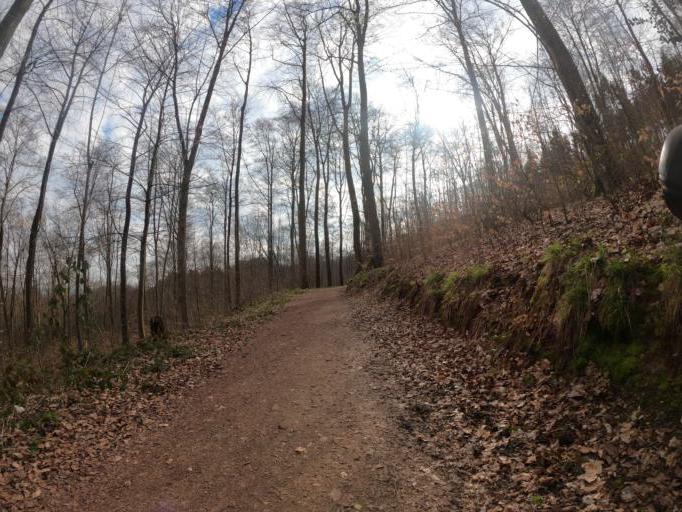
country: DE
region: North Rhine-Westphalia
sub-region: Regierungsbezirk Koln
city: Aachen
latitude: 50.7407
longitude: 6.0637
